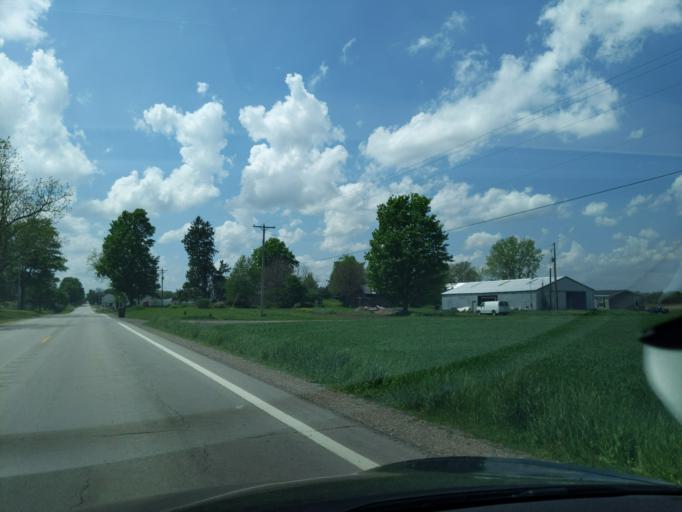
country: US
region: Michigan
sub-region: Ingham County
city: Williamston
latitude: 42.5559
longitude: -84.2892
